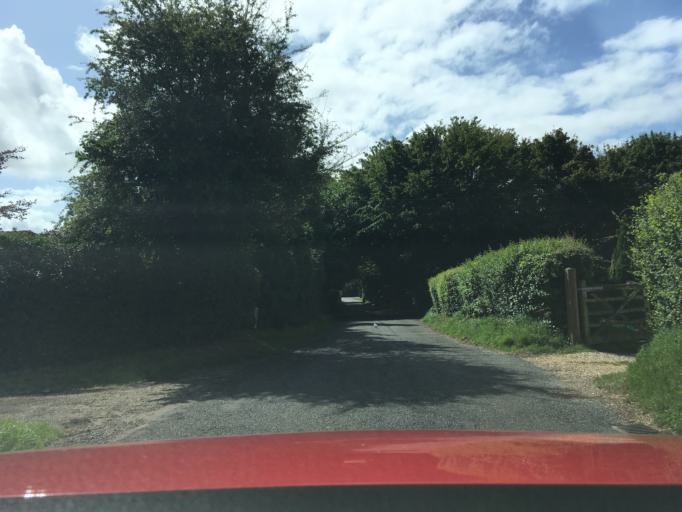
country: GB
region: England
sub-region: West Berkshire
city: Wickham
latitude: 51.4148
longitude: -1.4148
